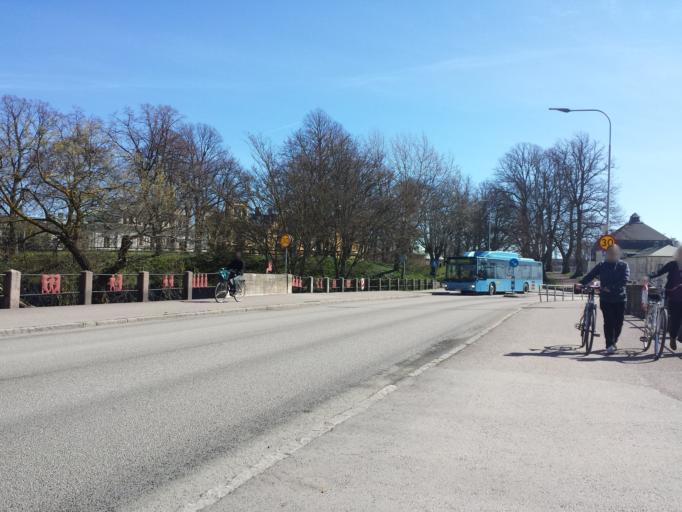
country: SE
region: Kalmar
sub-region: Kalmar Kommun
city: Kalmar
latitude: 56.6625
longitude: 16.3577
